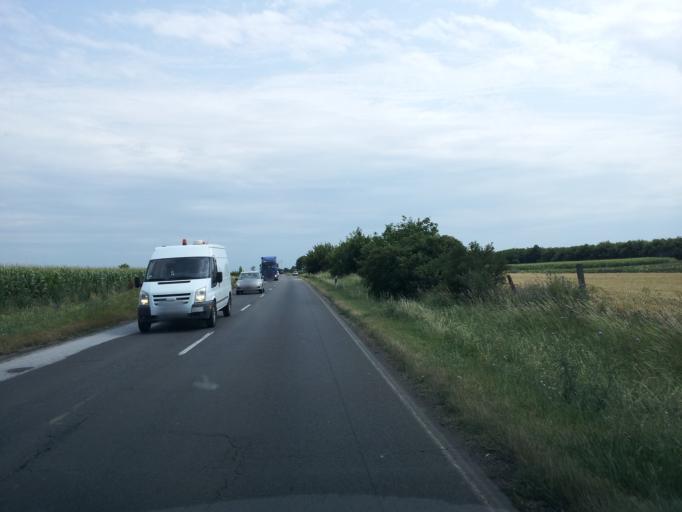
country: HU
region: Fejer
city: Lepseny
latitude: 46.9682
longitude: 18.2079
